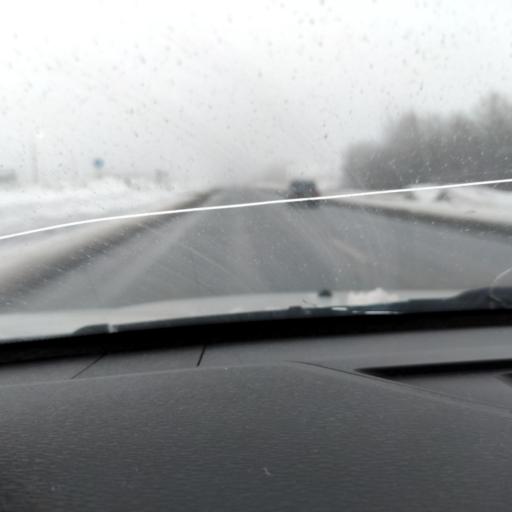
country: RU
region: Samara
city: Smyshlyayevka
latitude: 53.2599
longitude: 50.4372
